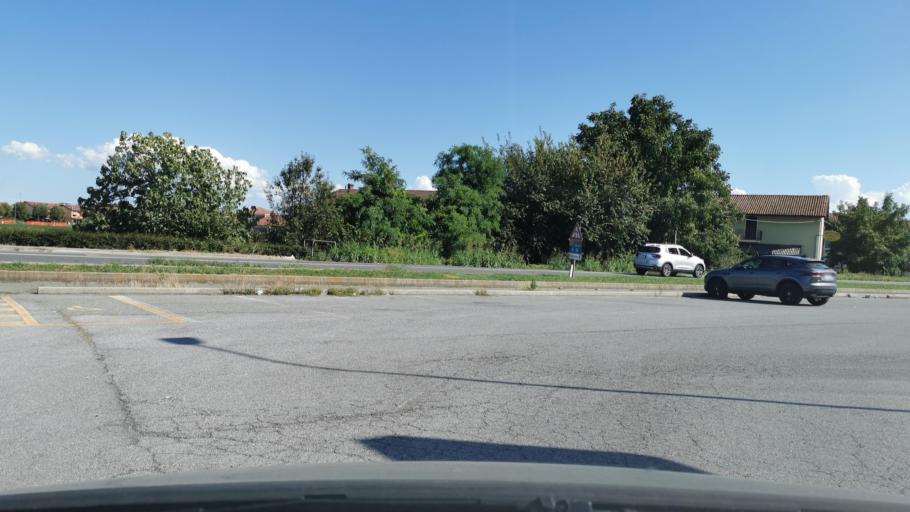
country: IT
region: Piedmont
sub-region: Provincia di Cuneo
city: Genola
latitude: 44.5922
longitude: 7.6568
